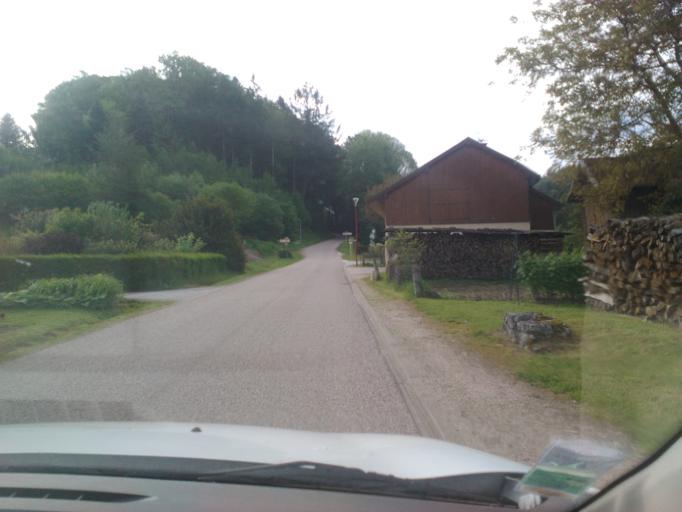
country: FR
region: Lorraine
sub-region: Departement des Vosges
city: Le Tholy
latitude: 48.1181
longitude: 6.7325
